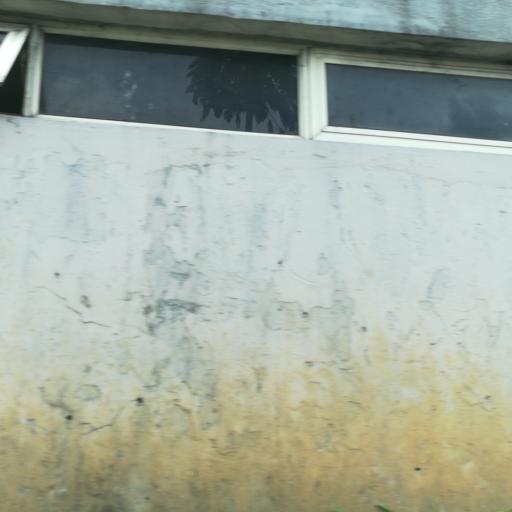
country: NG
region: Rivers
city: Port Harcourt
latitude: 4.7813
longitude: 7.0425
